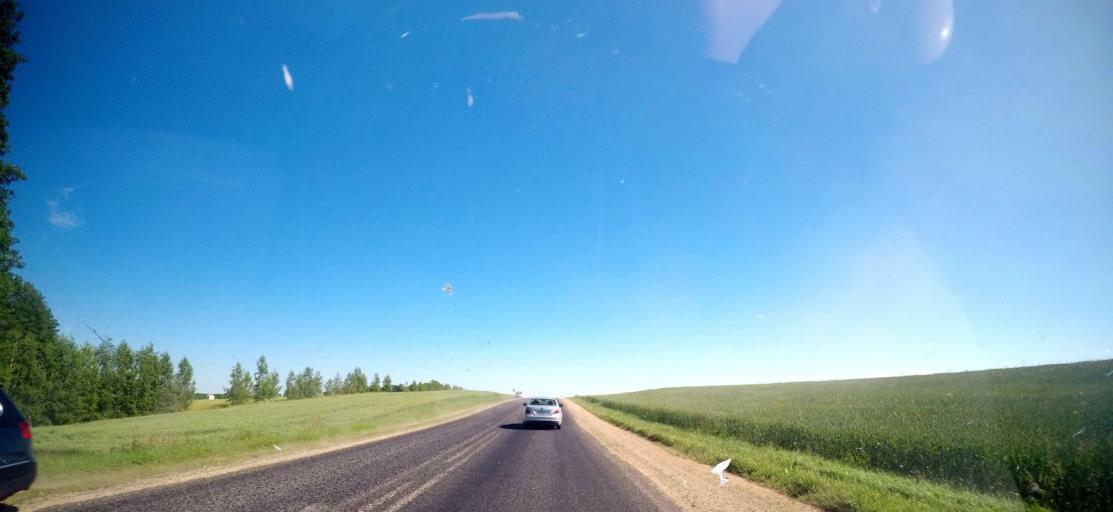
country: BY
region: Grodnenskaya
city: Vyalikaya Byerastavitsa
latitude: 53.2165
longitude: 23.9996
